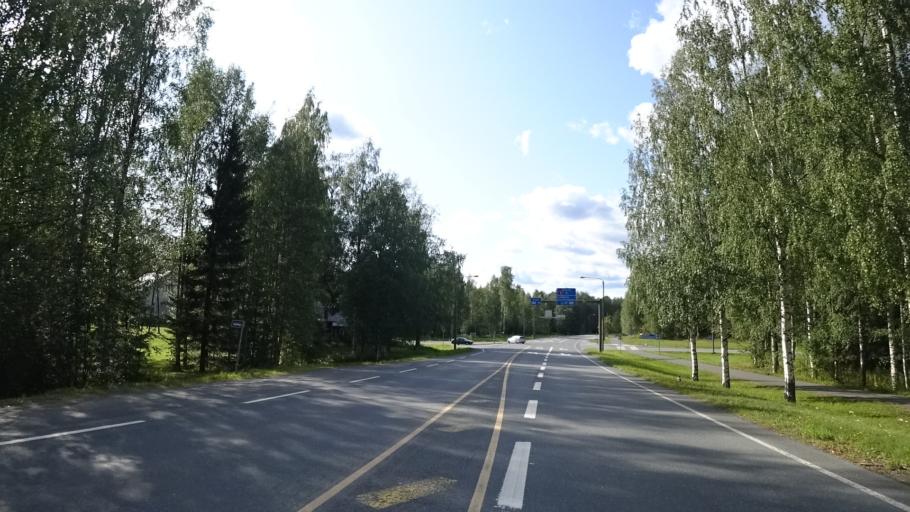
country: FI
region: North Karelia
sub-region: Keski-Karjala
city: Tohmajaervi
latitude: 62.2290
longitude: 30.3227
